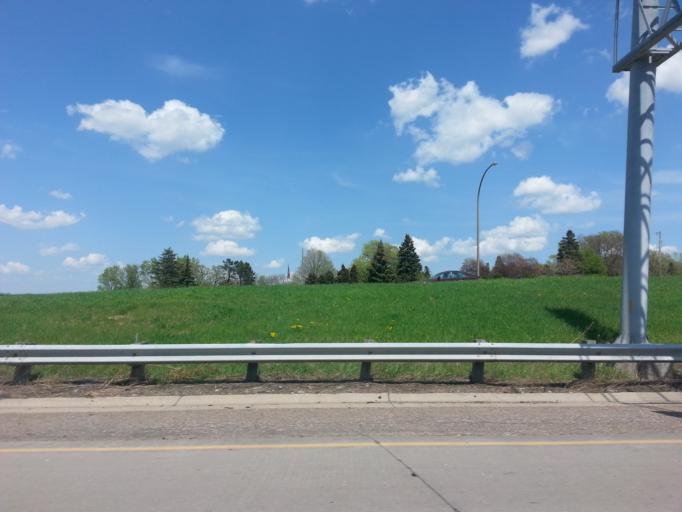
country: US
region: Minnesota
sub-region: Dakota County
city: Mendota Heights
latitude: 44.8827
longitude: -93.1683
